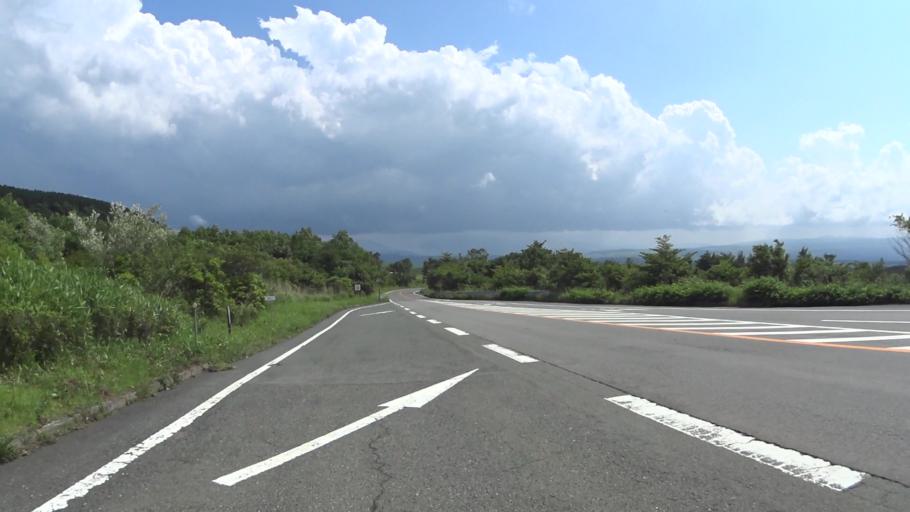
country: JP
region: Kumamoto
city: Aso
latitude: 33.0758
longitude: 131.1955
